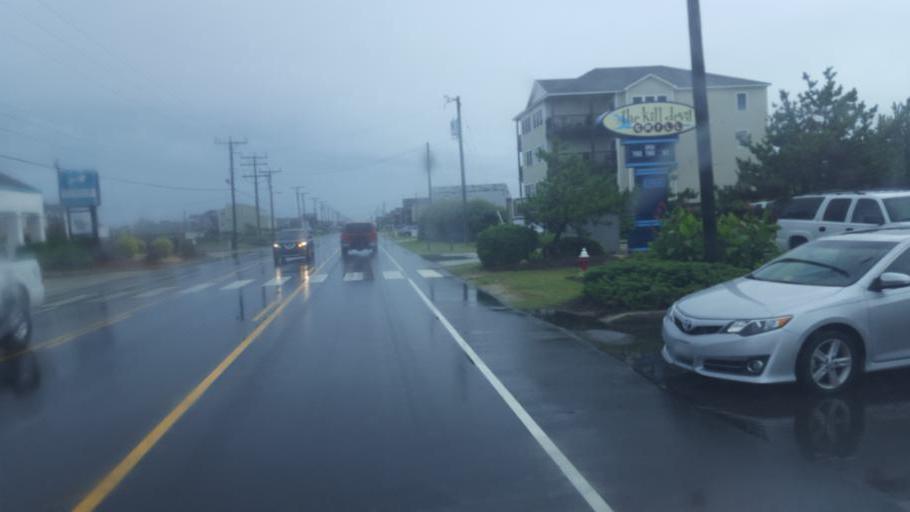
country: US
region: North Carolina
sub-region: Dare County
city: Kill Devil Hills
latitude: 35.9966
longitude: -75.6469
